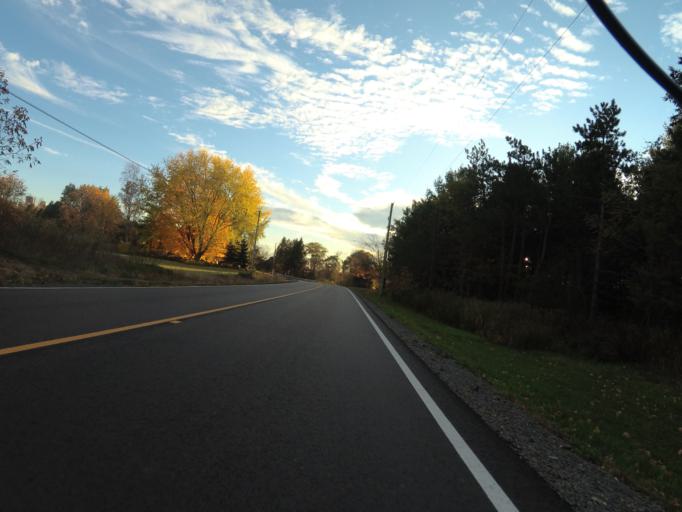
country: CA
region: Ontario
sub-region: Lanark County
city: Smiths Falls
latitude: 44.9575
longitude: -75.8141
